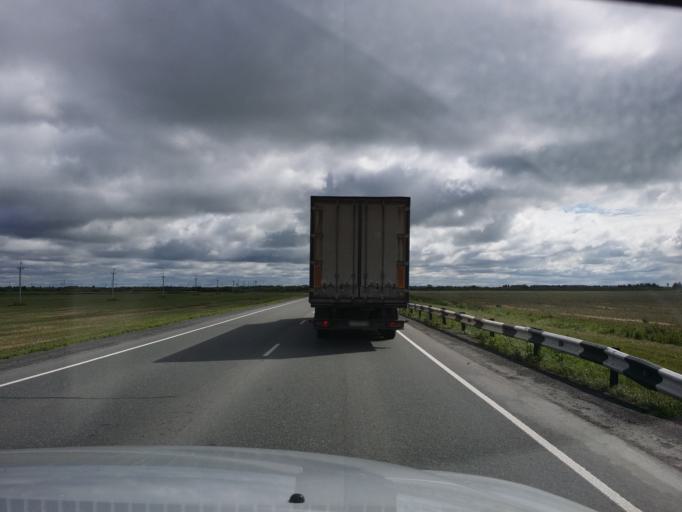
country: RU
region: Tjumen
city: Antipino
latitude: 57.1871
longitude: 65.9672
